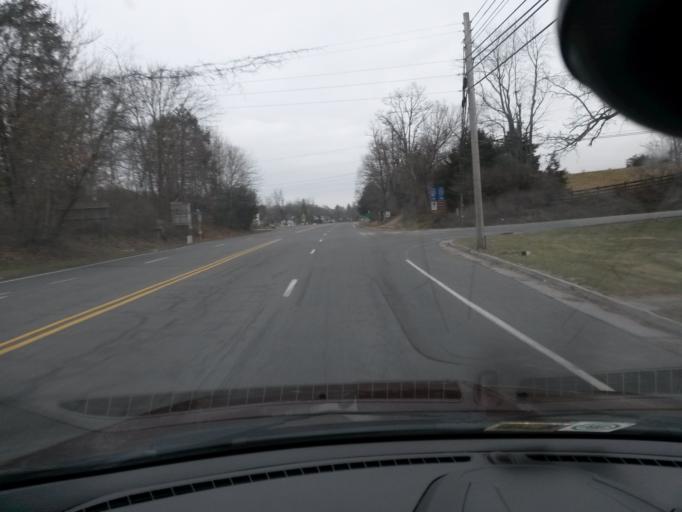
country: US
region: Virginia
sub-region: Augusta County
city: Stuarts Draft
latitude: 37.9247
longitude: -79.2036
